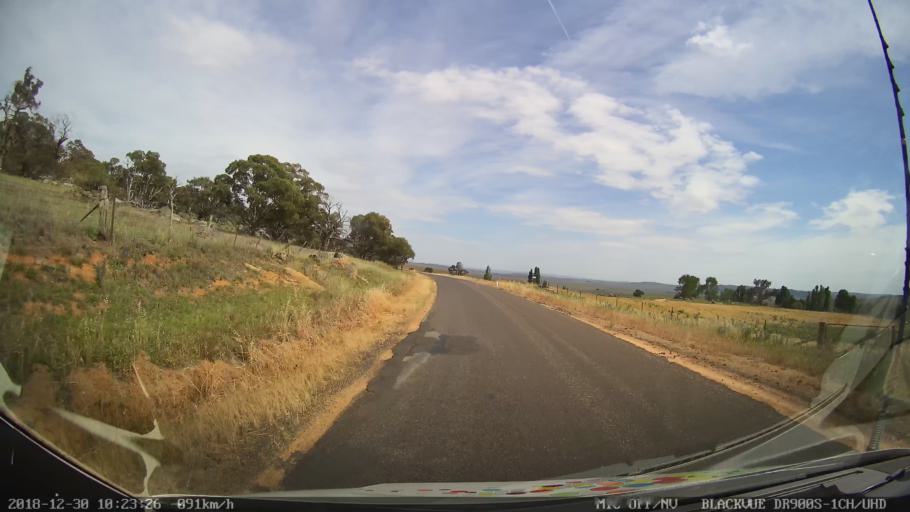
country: AU
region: New South Wales
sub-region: Snowy River
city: Berridale
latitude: -36.5373
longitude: 148.9820
